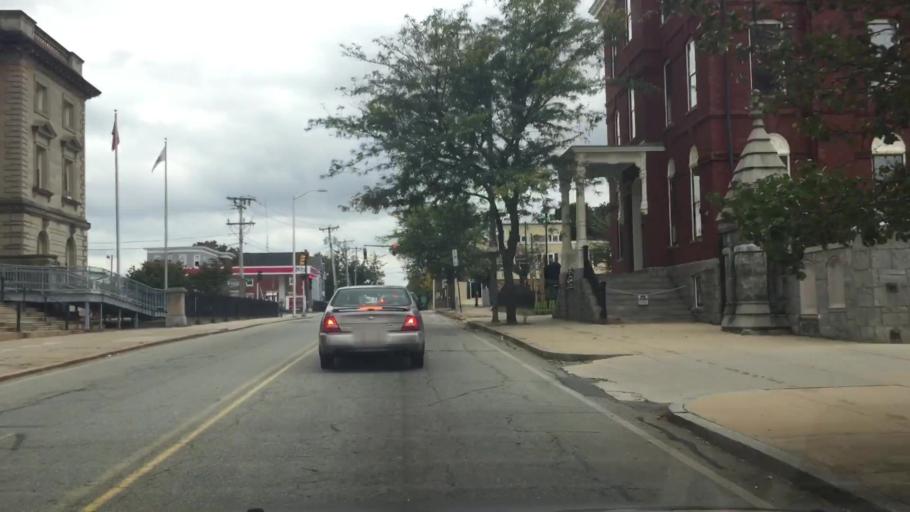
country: US
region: Massachusetts
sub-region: Middlesex County
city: Lowell
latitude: 42.6378
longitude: -71.3090
